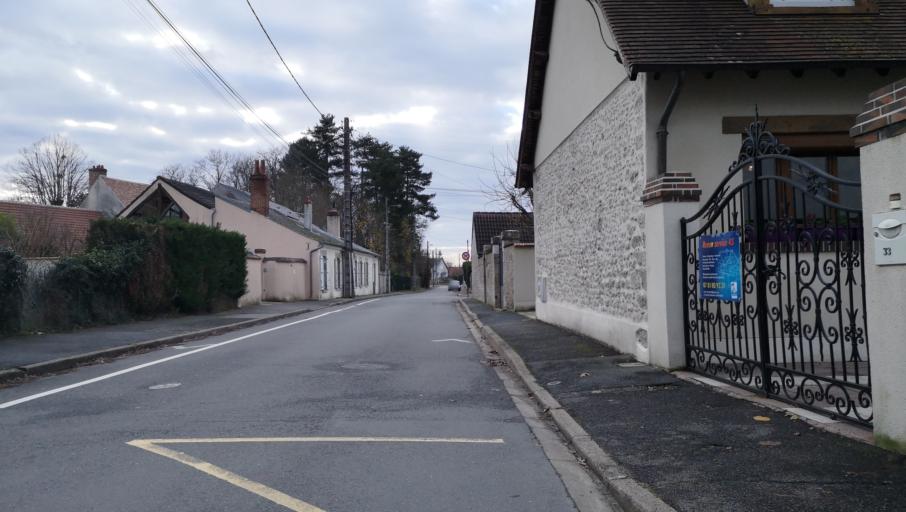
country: FR
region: Centre
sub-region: Departement du Loiret
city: Saint-Jean-de-Braye
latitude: 47.9098
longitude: 1.9832
